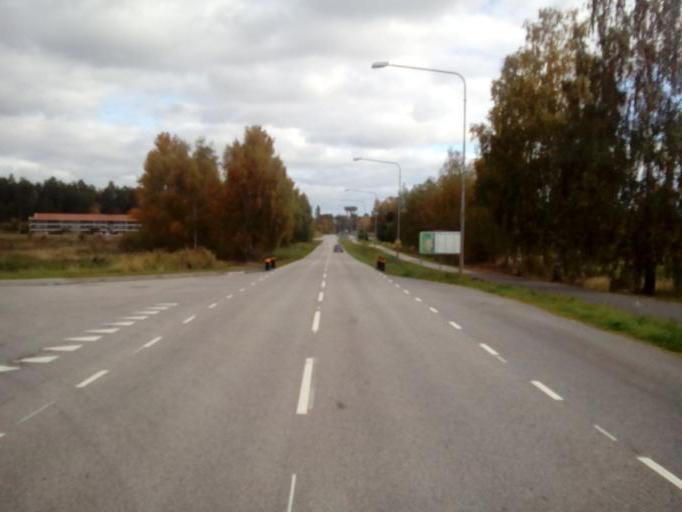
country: SE
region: Kalmar
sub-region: Vasterviks Kommun
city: Gamleby
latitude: 57.8917
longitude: 16.3914
